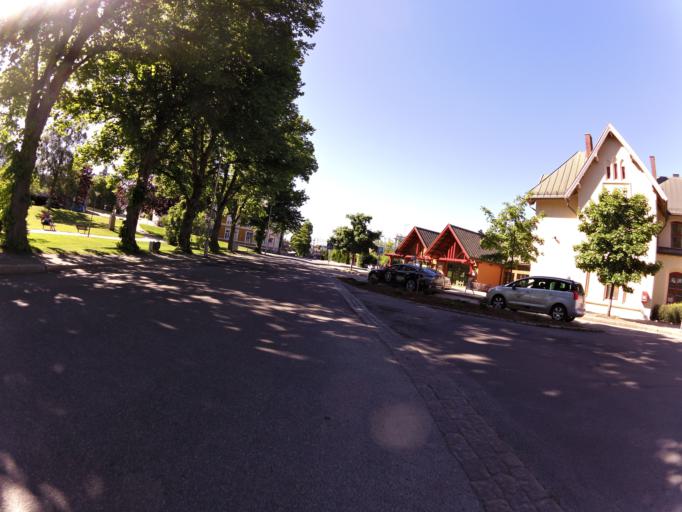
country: NO
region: Ostfold
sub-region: Fredrikstad
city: Fredrikstad
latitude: 59.2086
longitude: 10.9502
